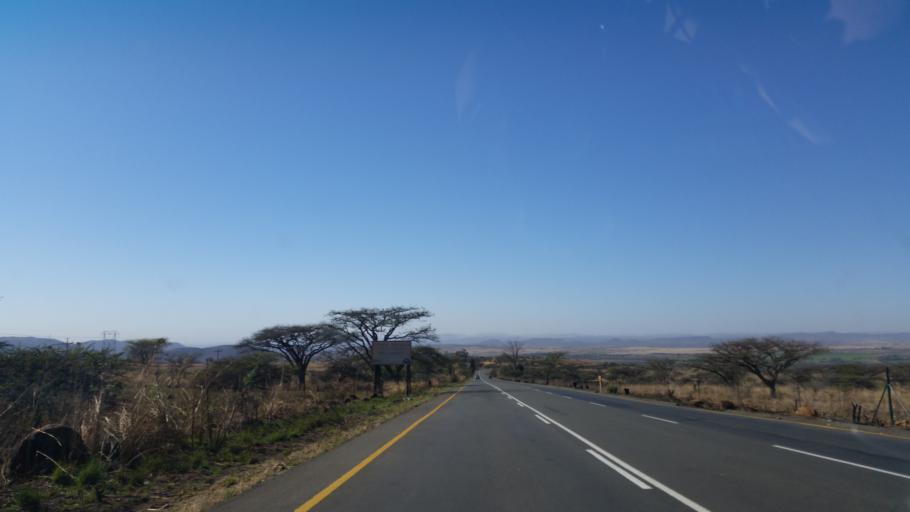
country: ZA
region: KwaZulu-Natal
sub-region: uThukela District Municipality
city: Ladysmith
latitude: -28.6977
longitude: 29.7705
